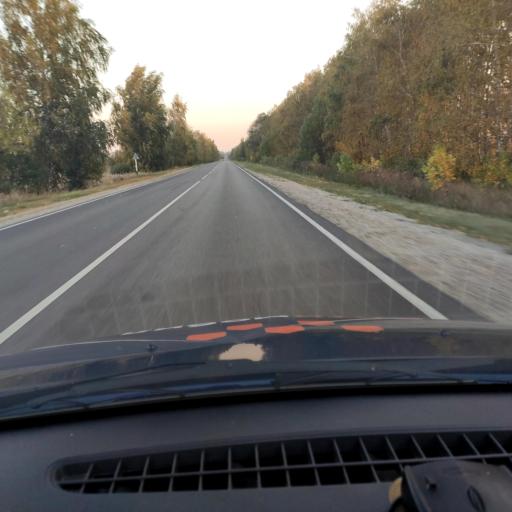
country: RU
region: Voronezj
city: Latnaya
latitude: 51.6360
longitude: 38.7843
